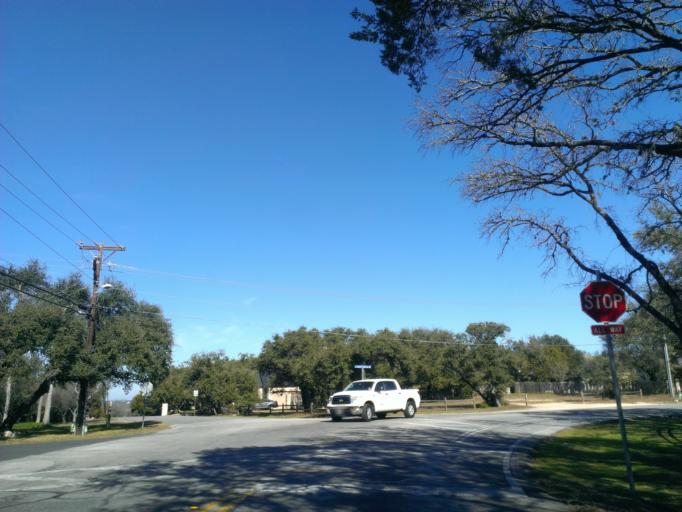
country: US
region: Texas
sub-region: Travis County
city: Lakeway
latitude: 30.3674
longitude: -97.9814
